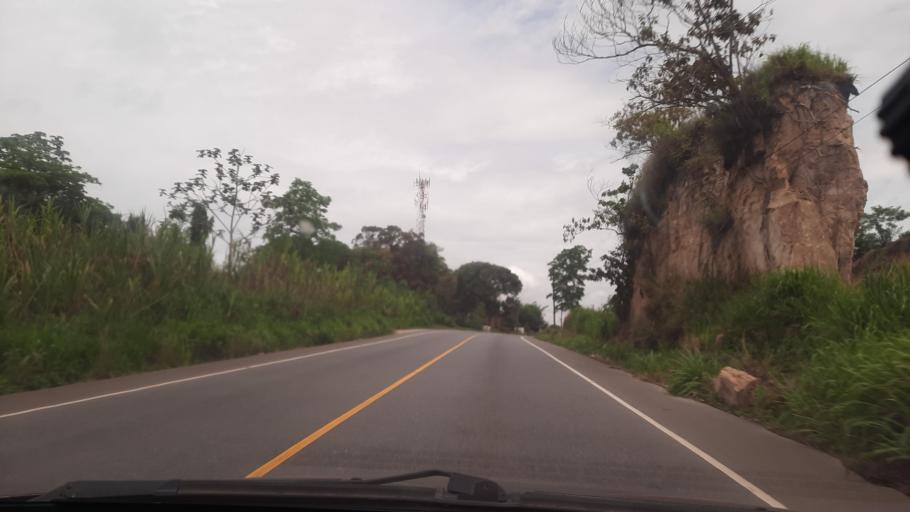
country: GT
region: Izabal
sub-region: Municipio de Los Amates
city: Los Amates
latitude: 15.2350
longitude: -89.1861
